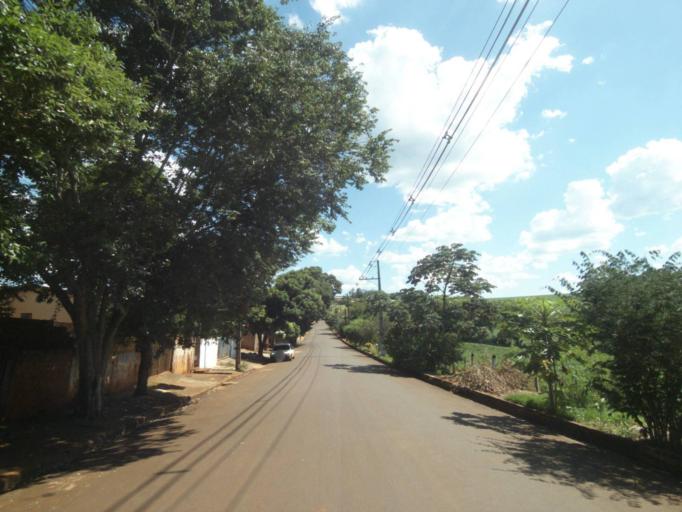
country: BR
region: Parana
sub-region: Sertanopolis
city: Sertanopolis
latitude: -23.0377
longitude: -50.8213
